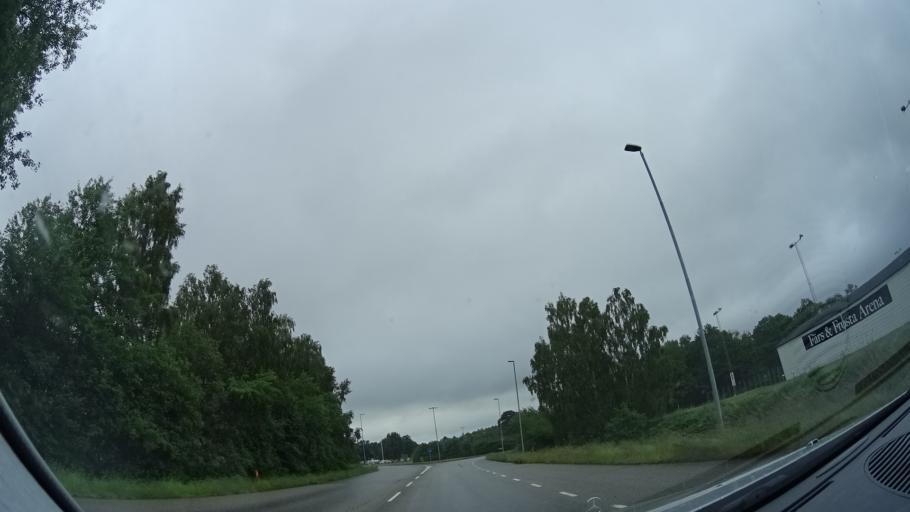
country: SE
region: Skane
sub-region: Hoors Kommun
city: Hoeoer
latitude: 55.9348
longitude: 13.5538
